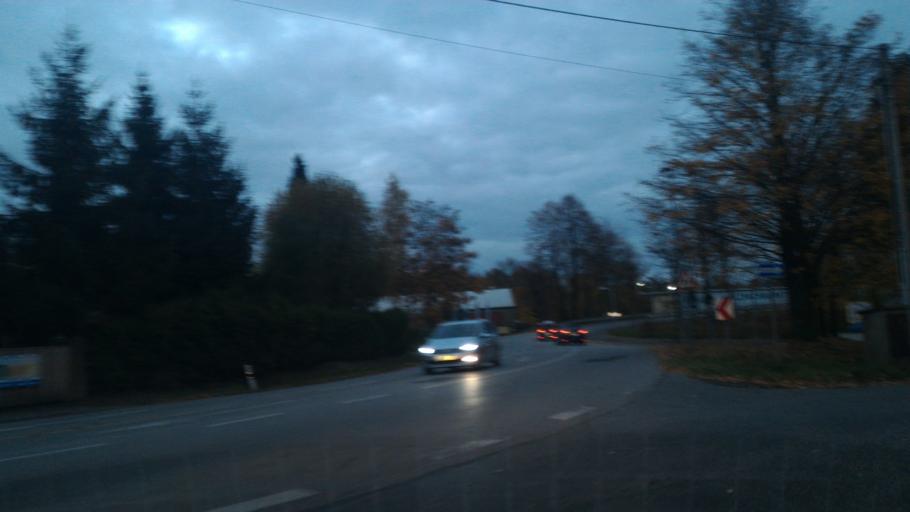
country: DE
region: Saxony
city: Neugersdorf
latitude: 50.9889
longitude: 14.6142
